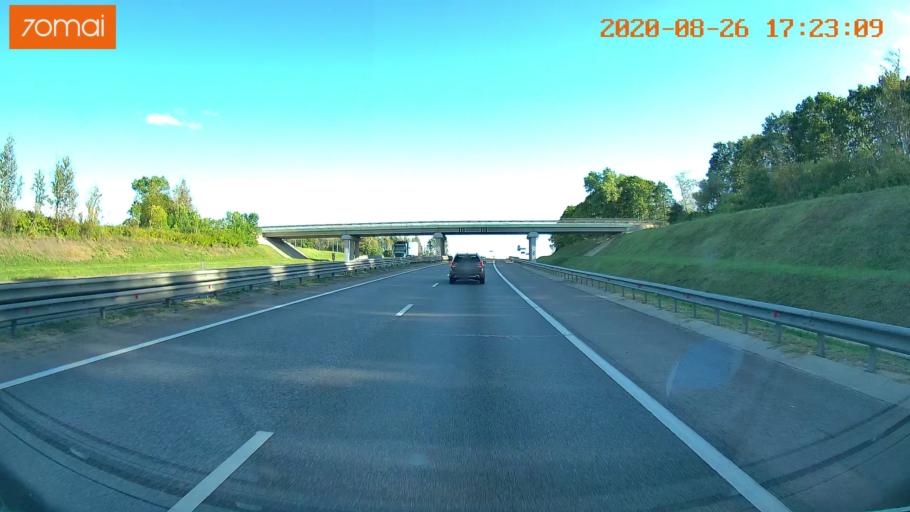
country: RU
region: Tula
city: Volovo
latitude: 53.5390
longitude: 38.1178
